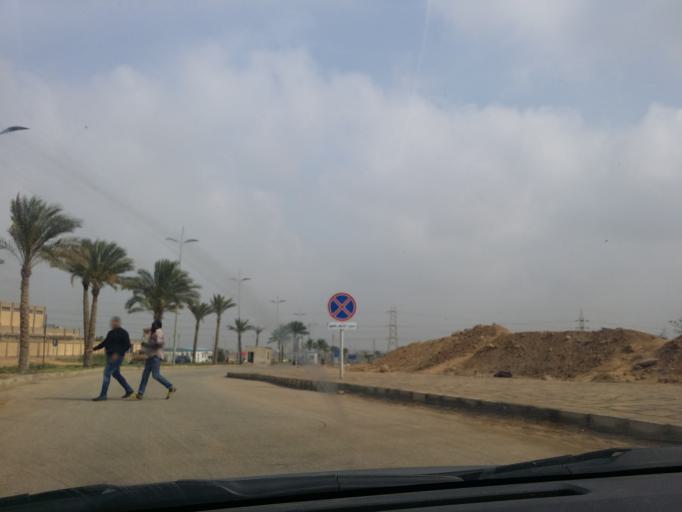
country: EG
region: Muhafazat al Qalyubiyah
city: Al Khankah
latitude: 30.1108
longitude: 31.6313
